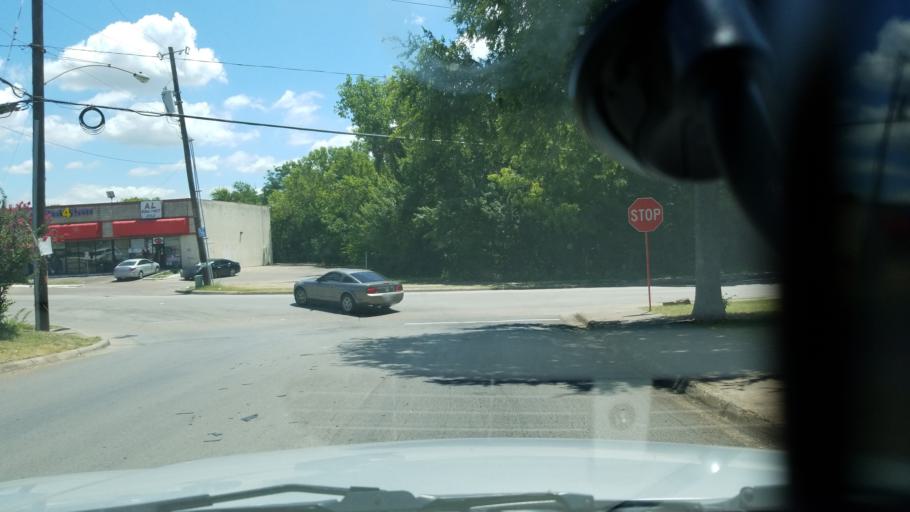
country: US
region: Texas
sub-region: Dallas County
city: Duncanville
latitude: 32.6609
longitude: -96.8682
